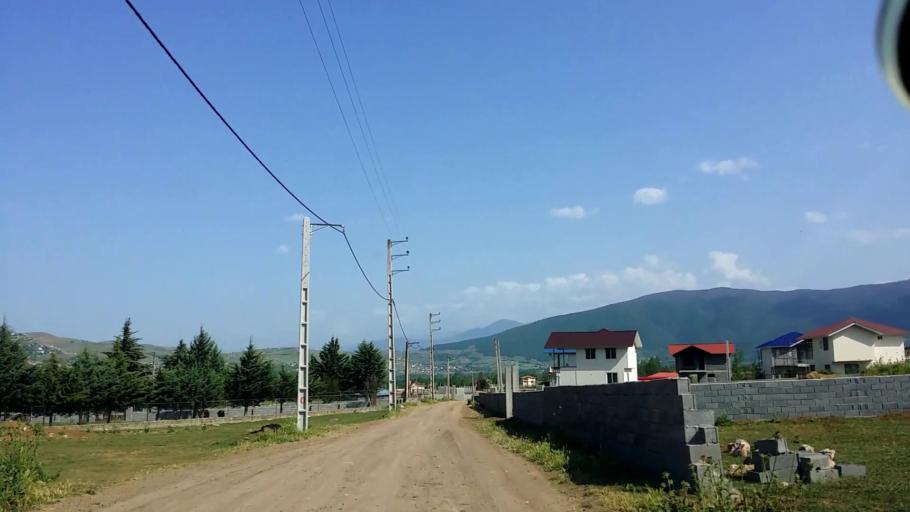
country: IR
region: Mazandaran
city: `Abbasabad
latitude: 36.5452
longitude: 51.1874
